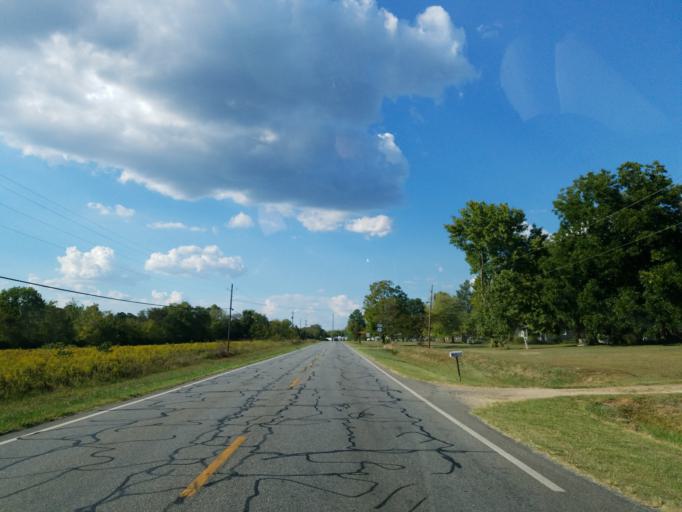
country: US
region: Georgia
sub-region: Bartow County
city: Rydal
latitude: 34.4927
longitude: -84.7080
